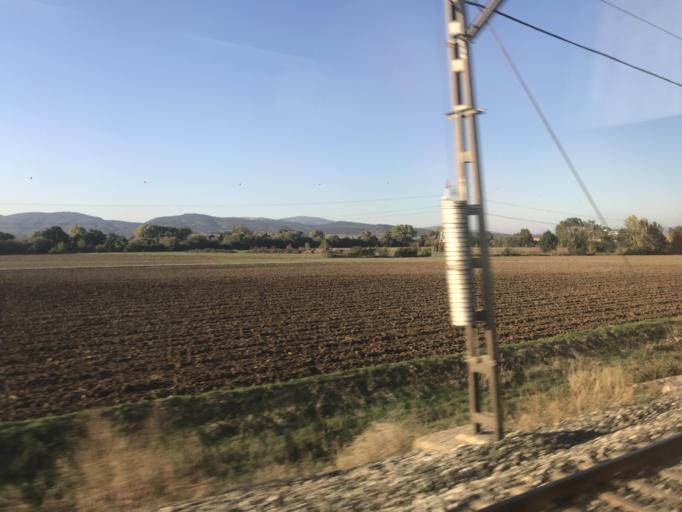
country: ES
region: Basque Country
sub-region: Provincia de Alava
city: Gasteiz / Vitoria
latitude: 42.8483
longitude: -2.7590
